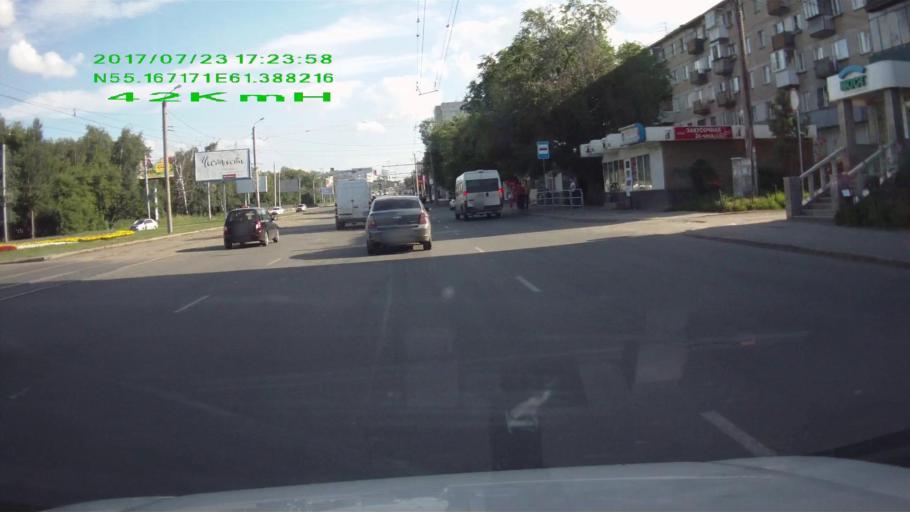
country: RU
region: Chelyabinsk
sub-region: Gorod Chelyabinsk
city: Chelyabinsk
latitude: 55.1668
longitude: 61.3882
